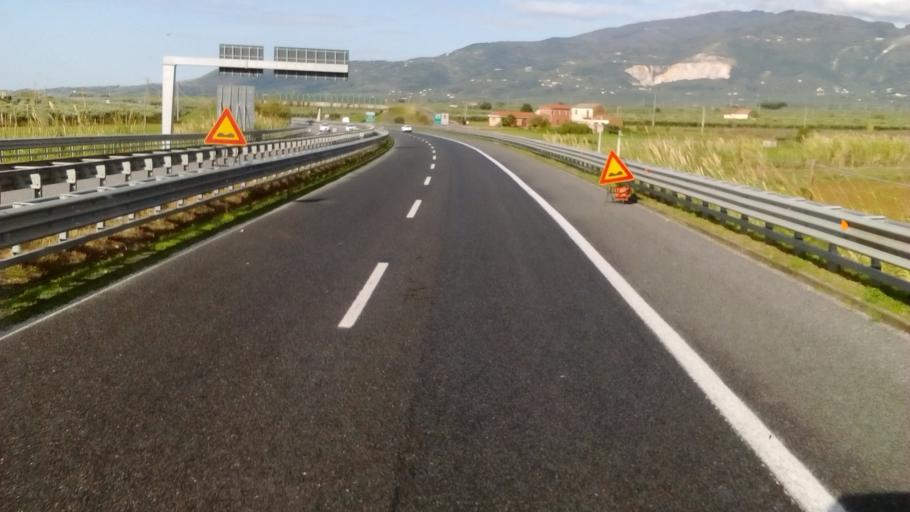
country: IT
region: Calabria
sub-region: Provincia di Catanzaro
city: Santa Eufemia Lamezia
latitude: 38.9209
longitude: 16.2627
